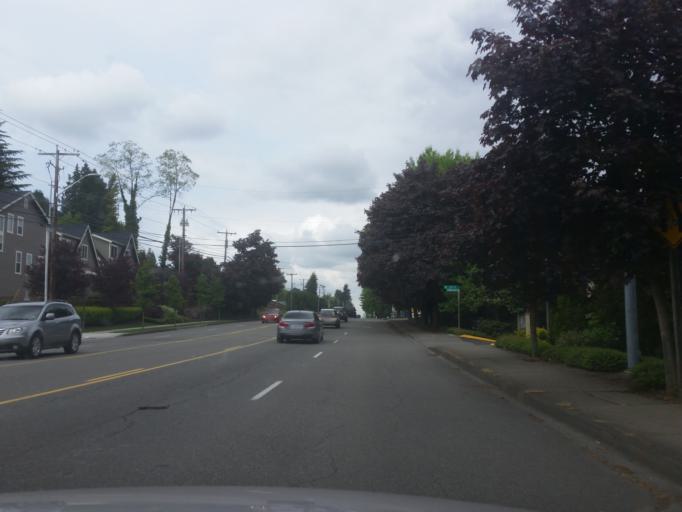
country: US
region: Washington
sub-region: King County
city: Inglewood-Finn Hill
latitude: 47.7239
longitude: -122.2077
